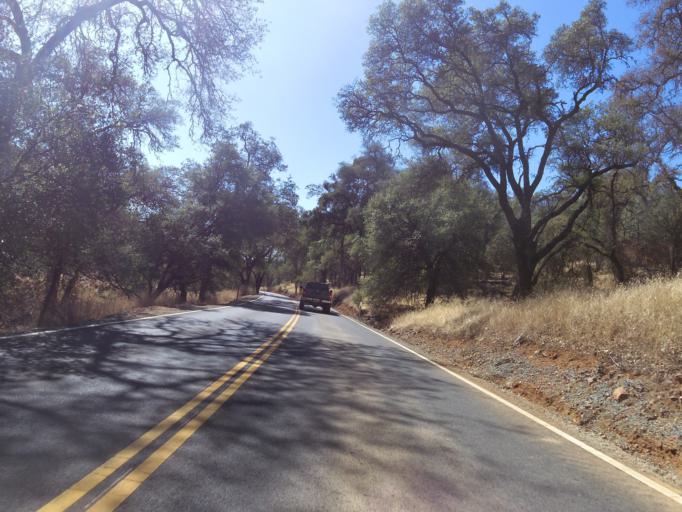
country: US
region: California
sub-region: El Dorado County
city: Deer Park
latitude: 38.6136
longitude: -120.8526
